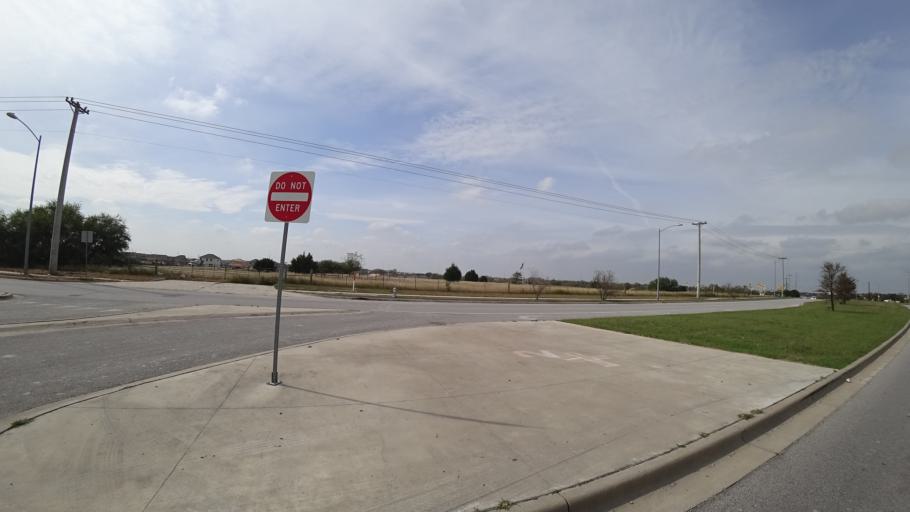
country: US
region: Texas
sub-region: Travis County
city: Windemere
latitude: 30.4350
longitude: -97.6541
